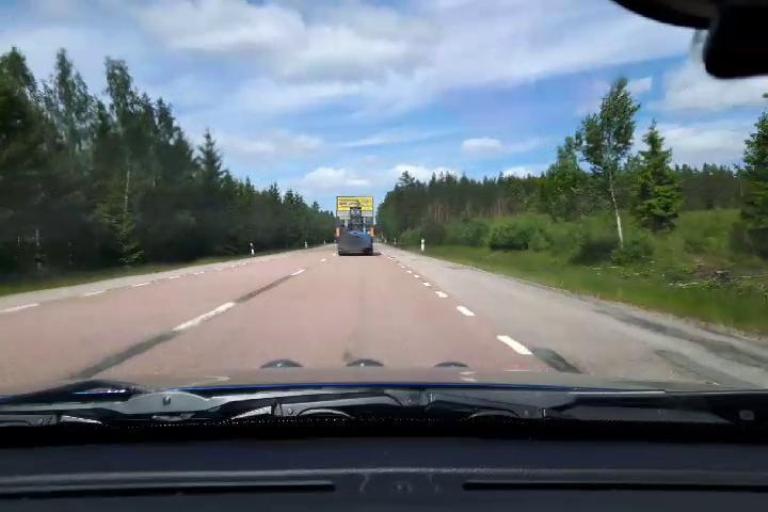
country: SE
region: Uppsala
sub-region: Osthammars Kommun
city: Bjorklinge
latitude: 60.1596
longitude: 17.4912
